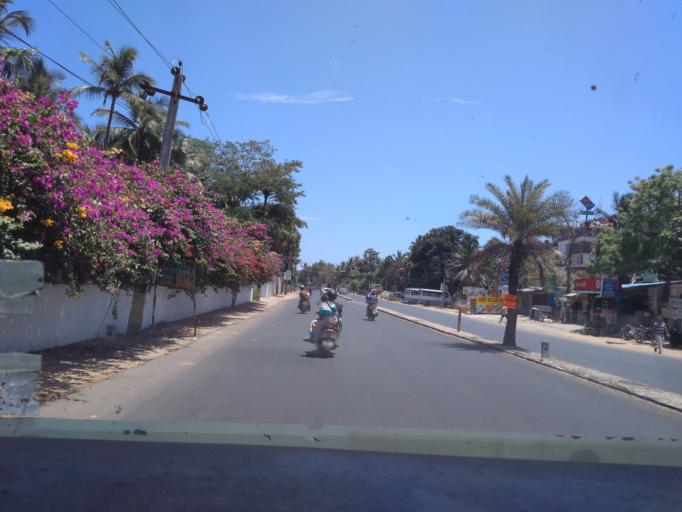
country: IN
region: Tamil Nadu
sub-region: Kancheepuram
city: Injambakkam
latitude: 12.8305
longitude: 80.2296
